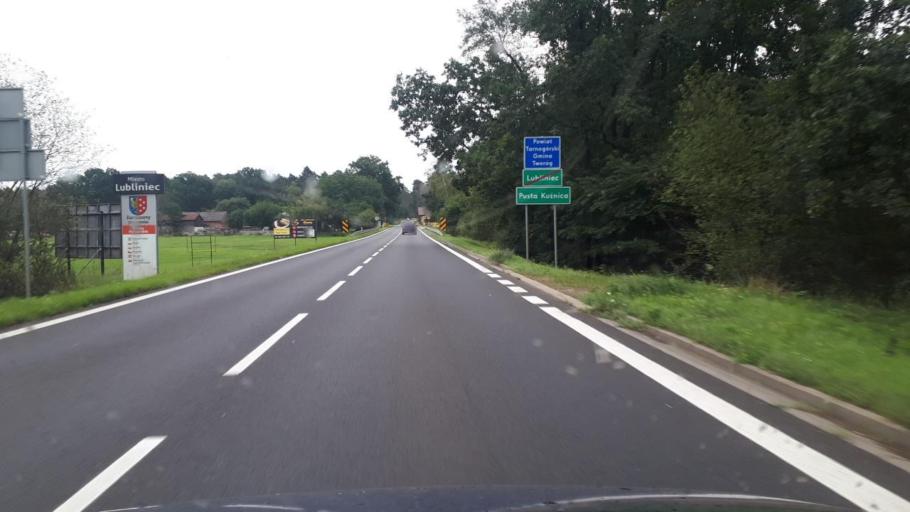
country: PL
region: Silesian Voivodeship
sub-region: Powiat tarnogorski
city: Tworog
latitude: 50.5882
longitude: 18.7032
